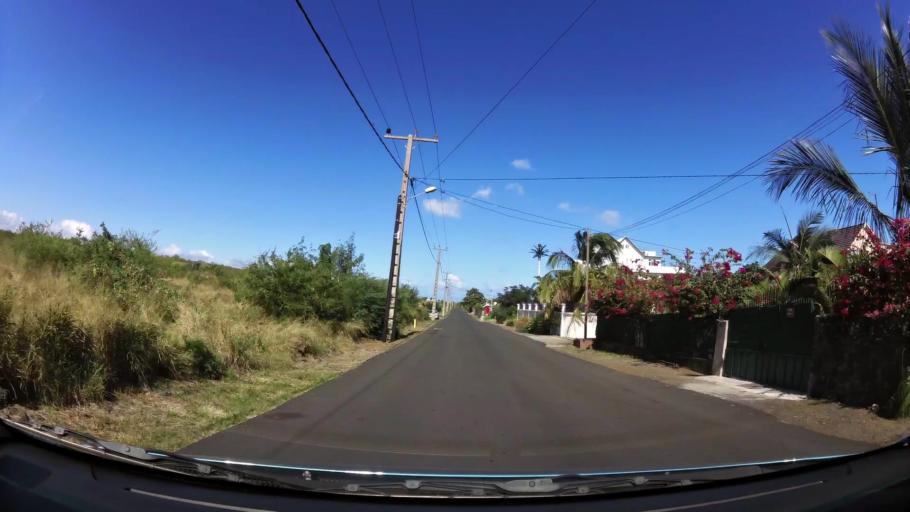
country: MU
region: Black River
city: Flic en Flac
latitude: -20.2692
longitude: 57.3771
